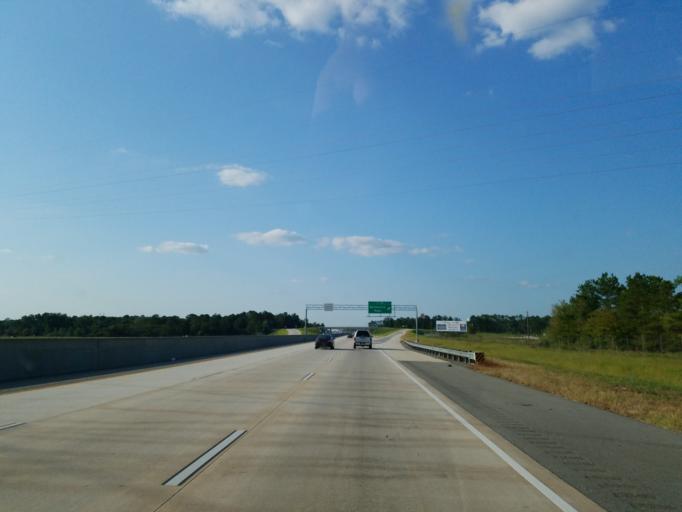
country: US
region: Georgia
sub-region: Cook County
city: Sparks
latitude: 31.2103
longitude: -83.4590
